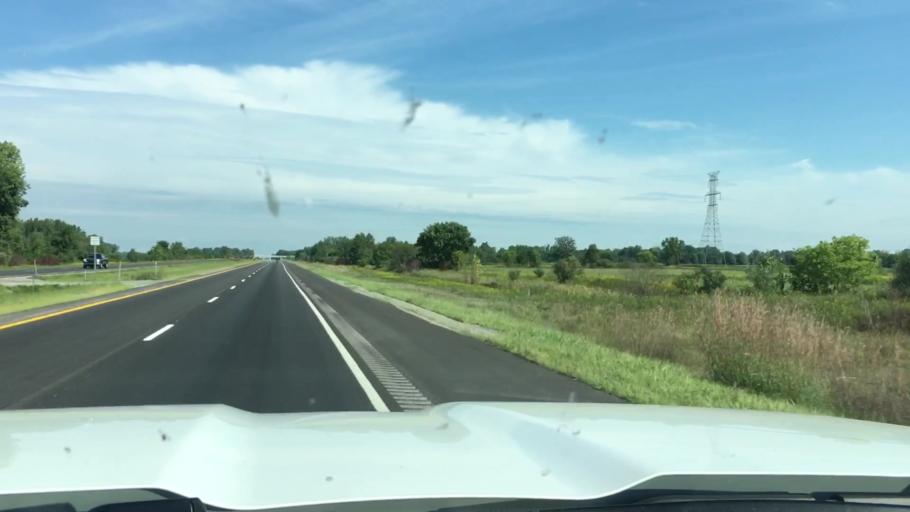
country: US
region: Michigan
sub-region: Saginaw County
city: Freeland
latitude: 43.5536
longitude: -84.1387
